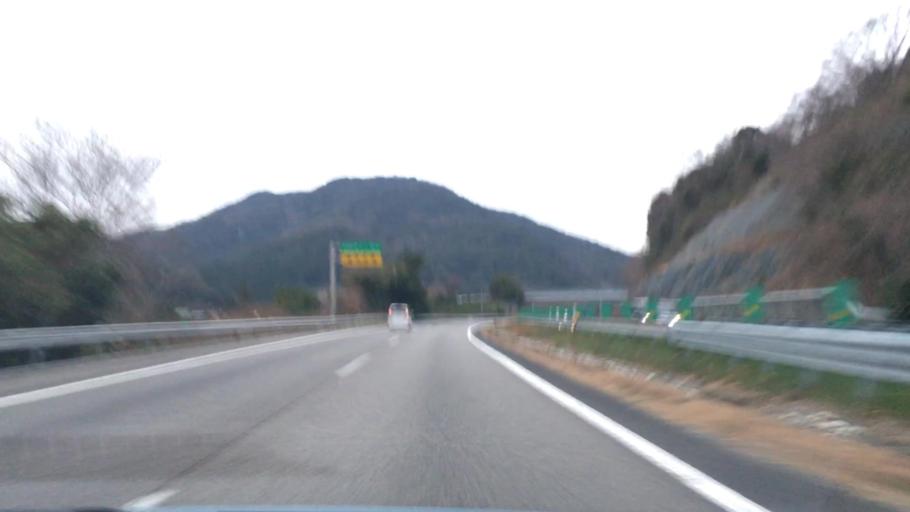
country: JP
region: Aichi
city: Shinshiro
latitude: 34.8327
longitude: 137.5367
